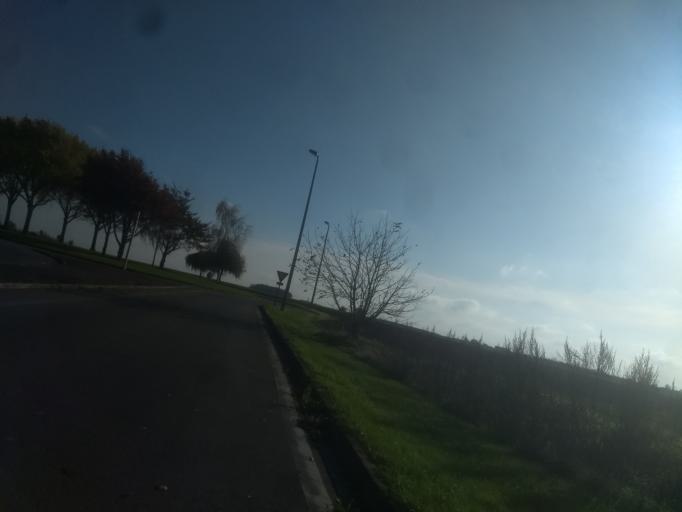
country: FR
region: Nord-Pas-de-Calais
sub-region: Departement du Pas-de-Calais
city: Beaurains
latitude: 50.2780
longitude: 2.7982
